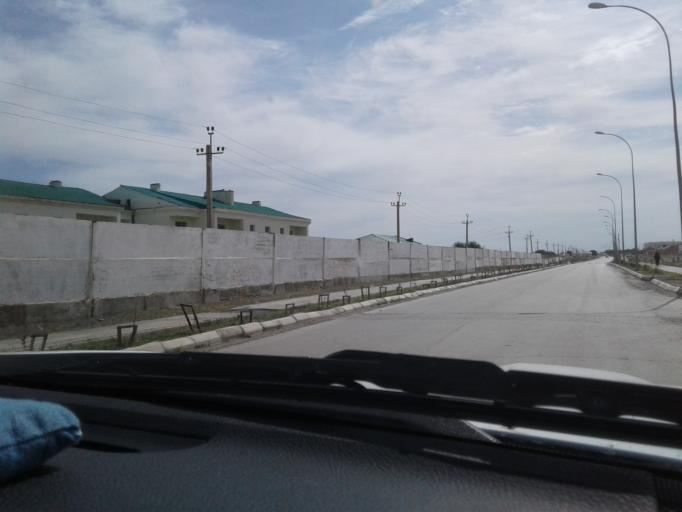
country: TM
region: Balkan
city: Gazanjyk
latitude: 39.2448
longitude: 55.4927
